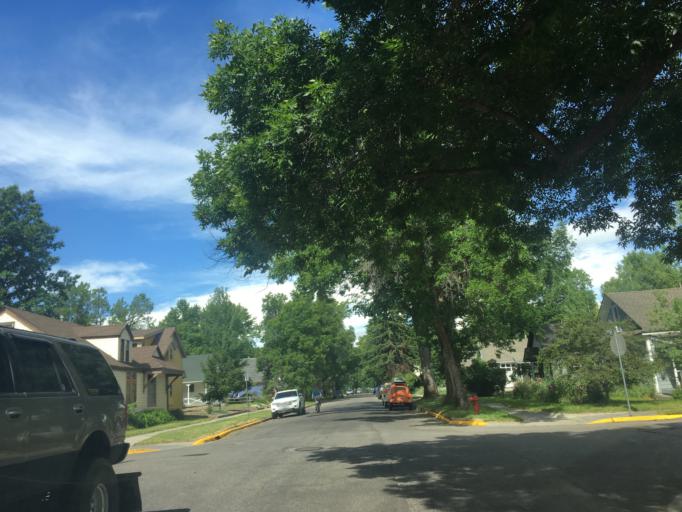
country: US
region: Montana
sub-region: Gallatin County
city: Bozeman
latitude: 45.6813
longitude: -111.0411
